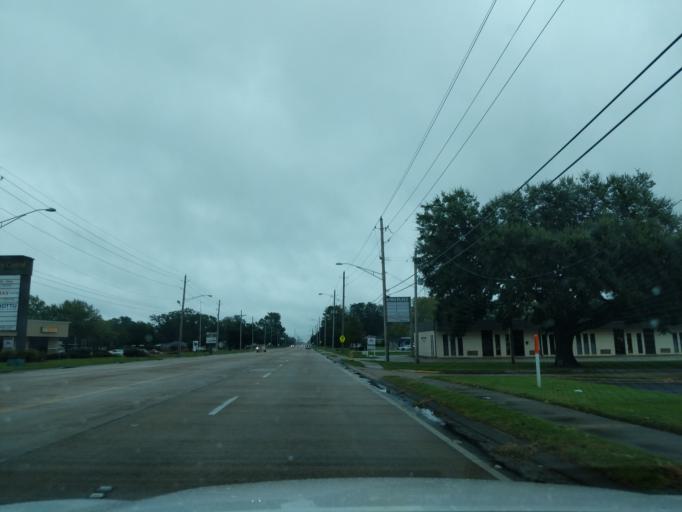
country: US
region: Louisiana
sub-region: Bossier Parish
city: Bossier City
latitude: 32.5187
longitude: -93.7061
